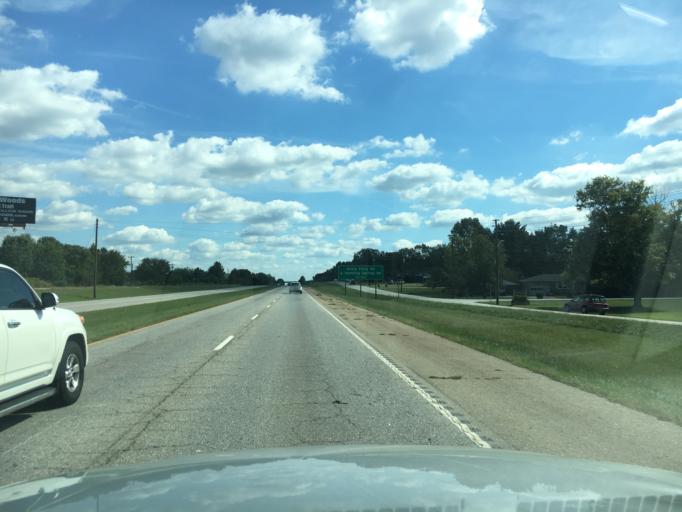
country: US
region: South Carolina
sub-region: Greenville County
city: Mauldin
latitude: 34.7670
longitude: -82.2977
